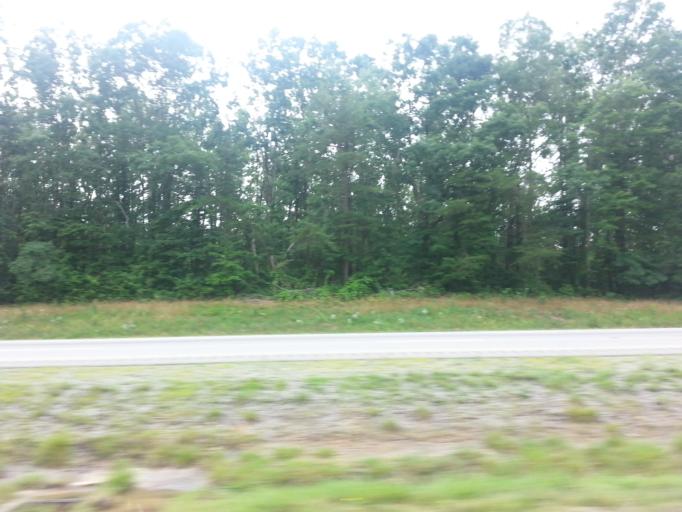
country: US
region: Tennessee
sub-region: Putnam County
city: Monterey
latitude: 36.1209
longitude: -85.2515
